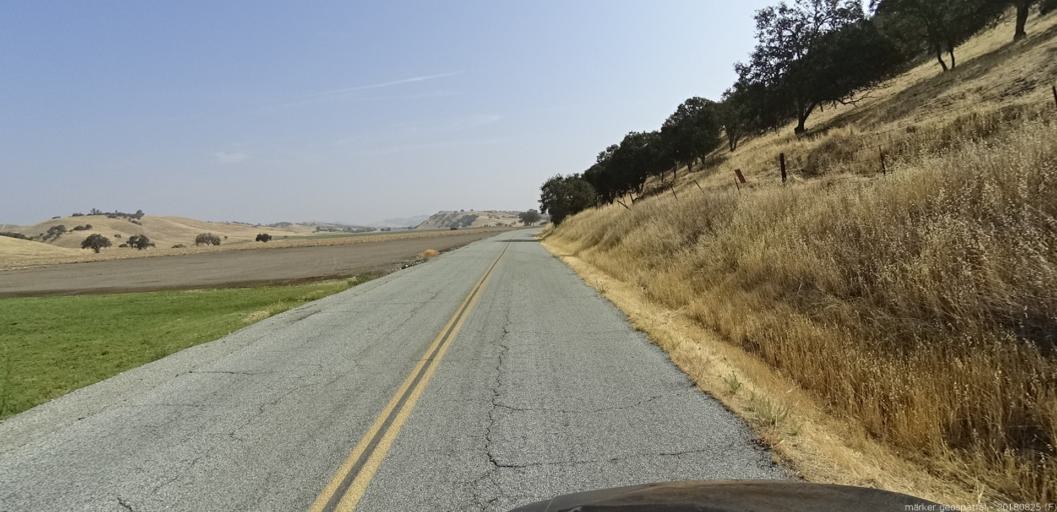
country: US
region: California
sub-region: San Luis Obispo County
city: San Miguel
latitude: 35.8148
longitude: -120.6647
